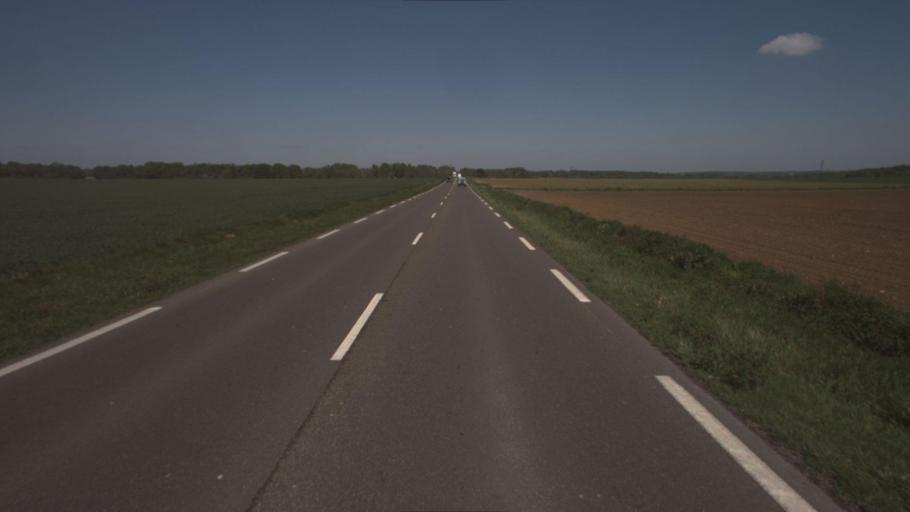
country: FR
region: Ile-de-France
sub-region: Departement de Seine-et-Marne
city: Villiers-sur-Morin
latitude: 48.8389
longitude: 2.8743
